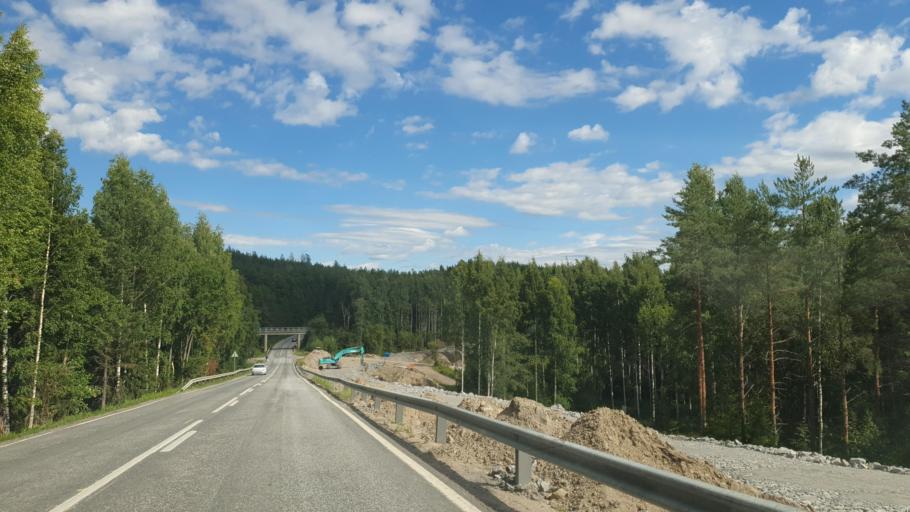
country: FI
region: Central Finland
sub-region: Jyvaeskylae
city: Muurame
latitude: 62.1448
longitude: 25.7077
